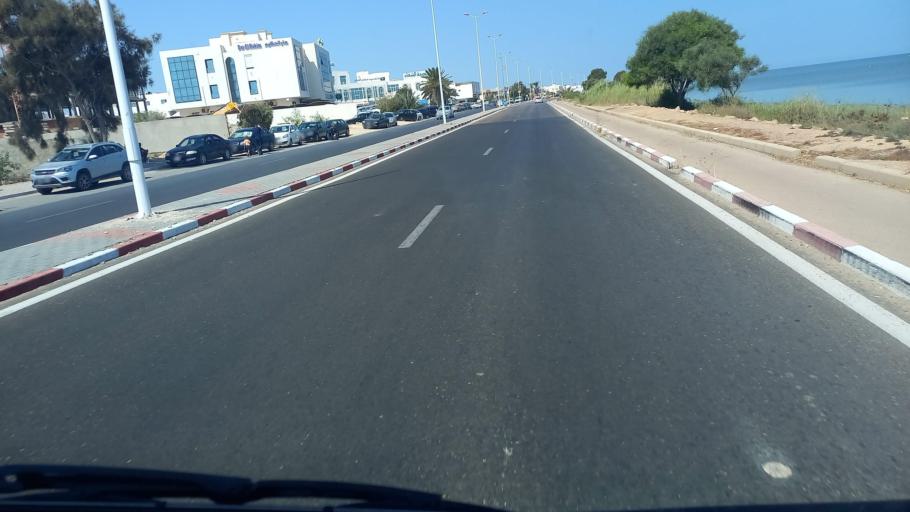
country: TN
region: Madanin
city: Houmt Souk
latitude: 33.8748
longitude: 10.8935
